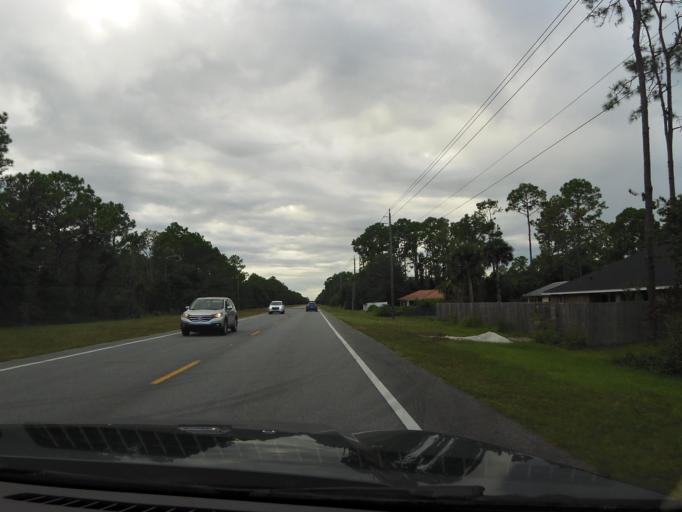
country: US
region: Florida
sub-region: Flagler County
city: Bunnell
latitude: 29.4976
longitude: -81.2251
